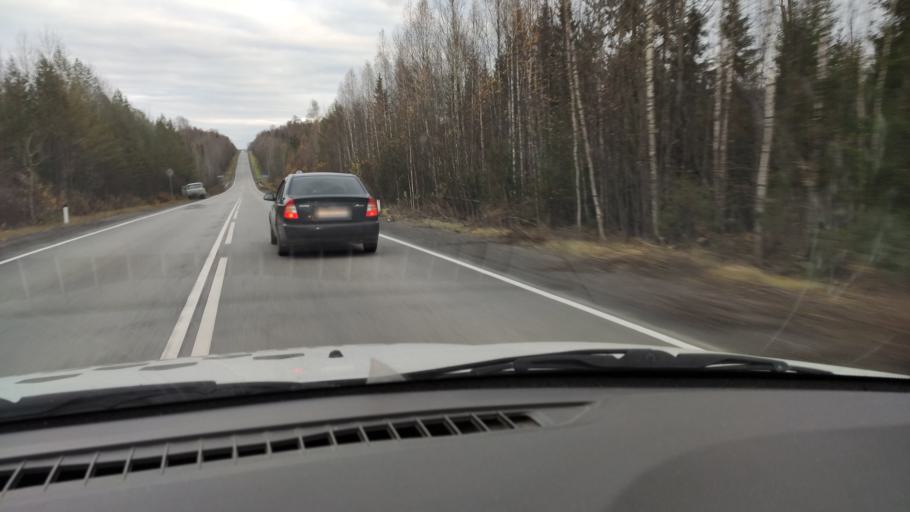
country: RU
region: Kirov
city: Chernaya Kholunitsa
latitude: 58.8651
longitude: 51.5795
